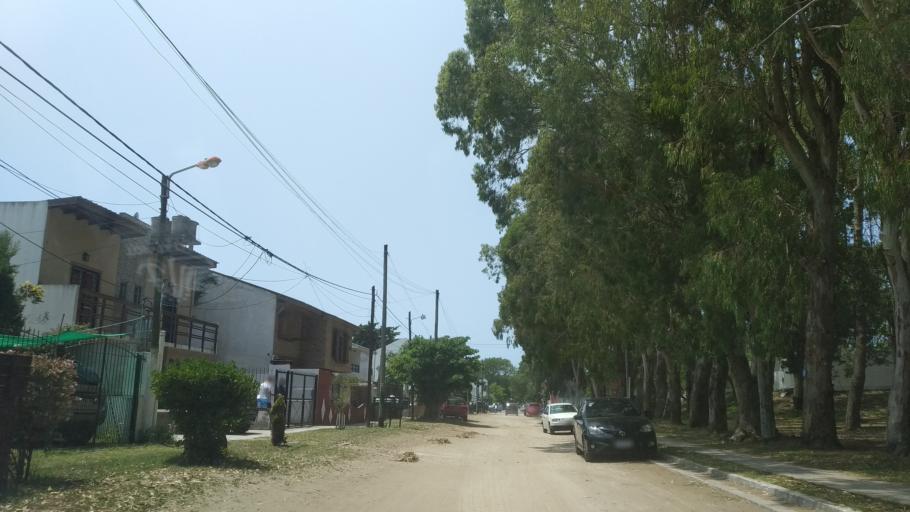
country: AR
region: Buenos Aires
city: Mar del Tuyu
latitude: -36.5570
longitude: -56.6943
